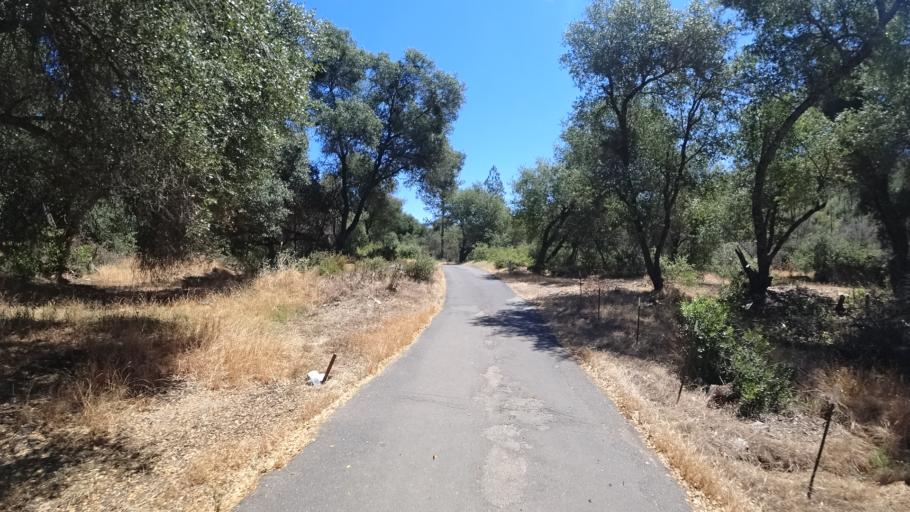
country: US
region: California
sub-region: Calaveras County
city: Mountain Ranch
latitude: 38.1834
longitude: -120.5778
